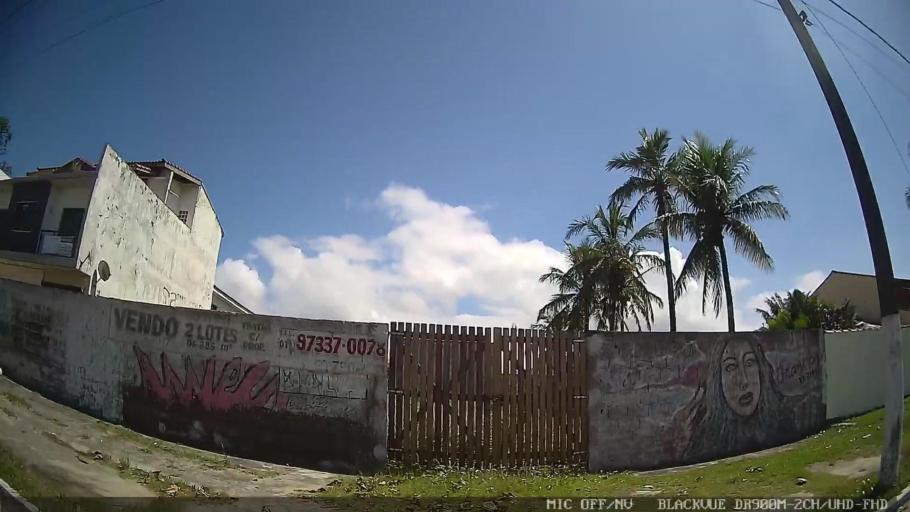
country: BR
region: Sao Paulo
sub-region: Peruibe
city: Peruibe
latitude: -24.3210
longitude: -46.9918
